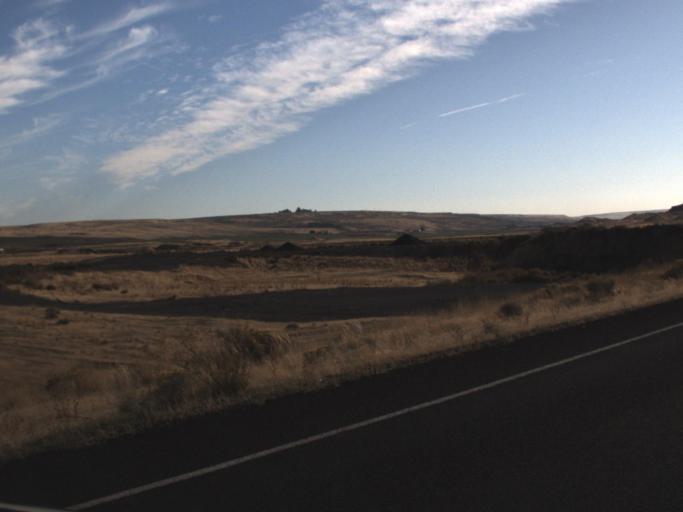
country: US
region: Washington
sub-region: Franklin County
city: Connell
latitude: 46.6476
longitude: -118.8411
